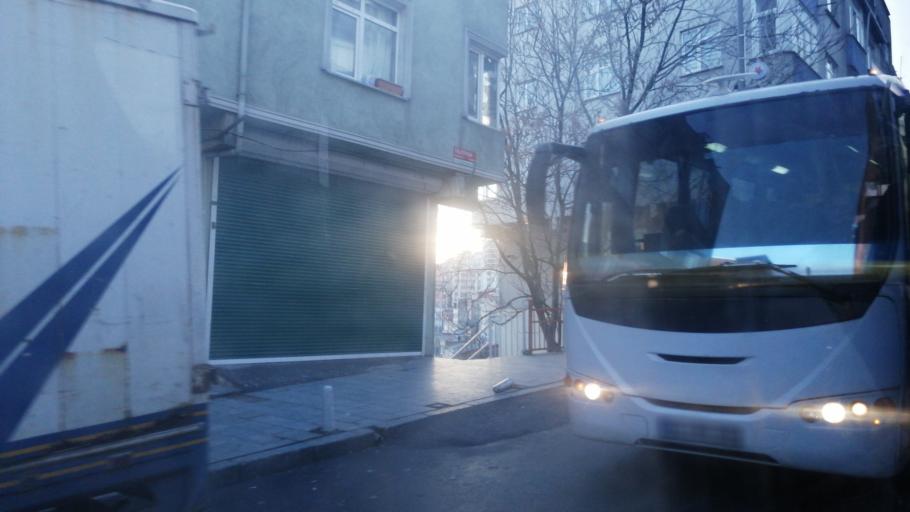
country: TR
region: Istanbul
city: Sisli
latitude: 41.0863
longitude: 28.9861
